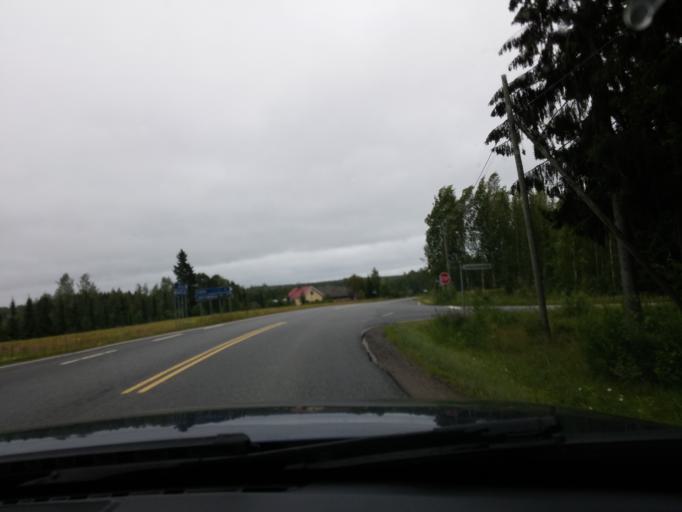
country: FI
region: Central Finland
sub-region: Joutsa
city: Joutsa
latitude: 61.7880
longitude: 26.0317
